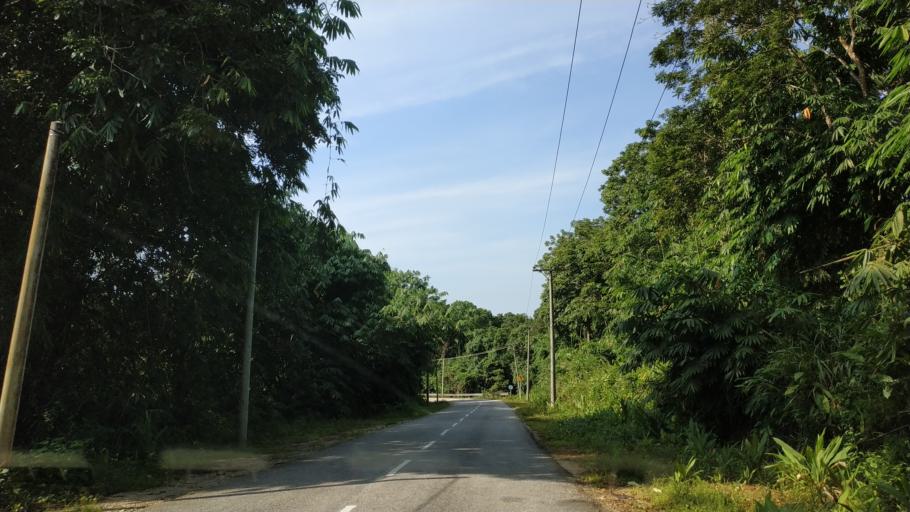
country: TH
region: Kanchanaburi
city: Thong Pha Phum
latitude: 14.6155
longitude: 98.1116
